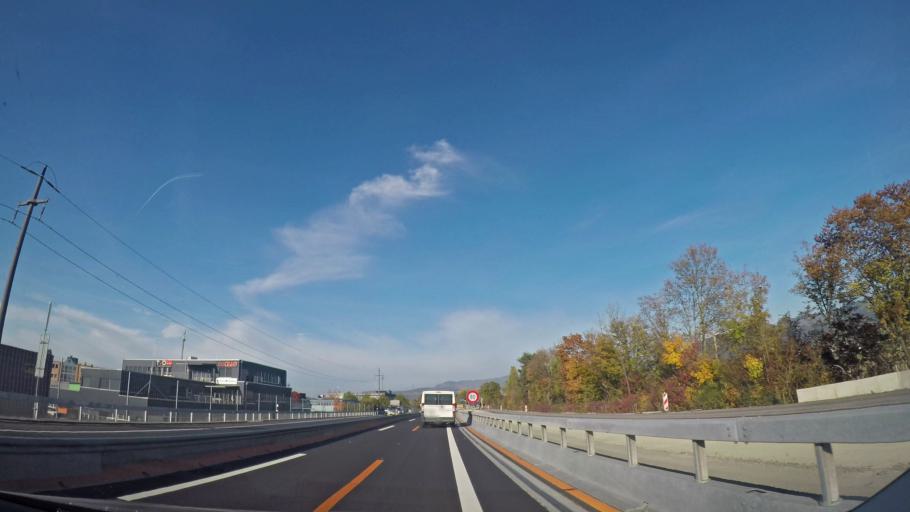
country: CH
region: Bern
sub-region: Thun District
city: Thun
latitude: 46.7385
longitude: 7.6010
